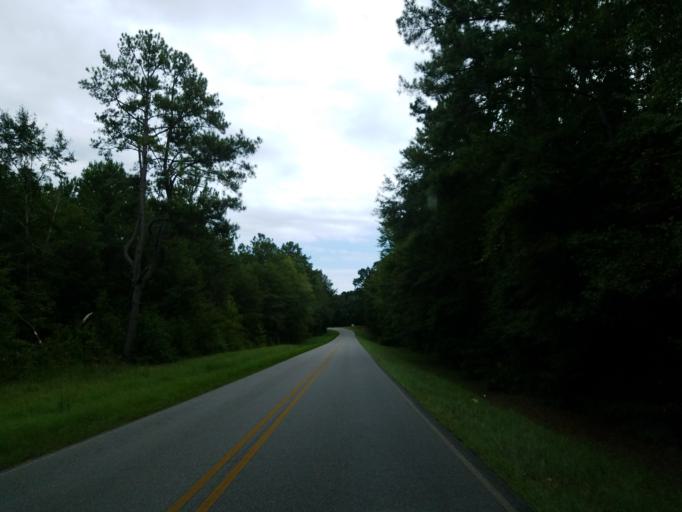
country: US
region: Georgia
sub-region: Monroe County
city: Forsyth
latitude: 32.9535
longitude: -83.9532
